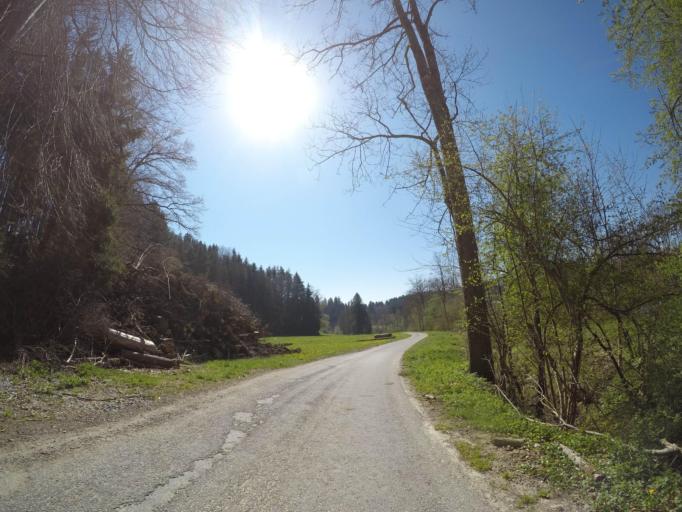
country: DE
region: Baden-Wuerttemberg
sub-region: Tuebingen Region
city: Horgenzell
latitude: 47.8205
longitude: 9.4611
